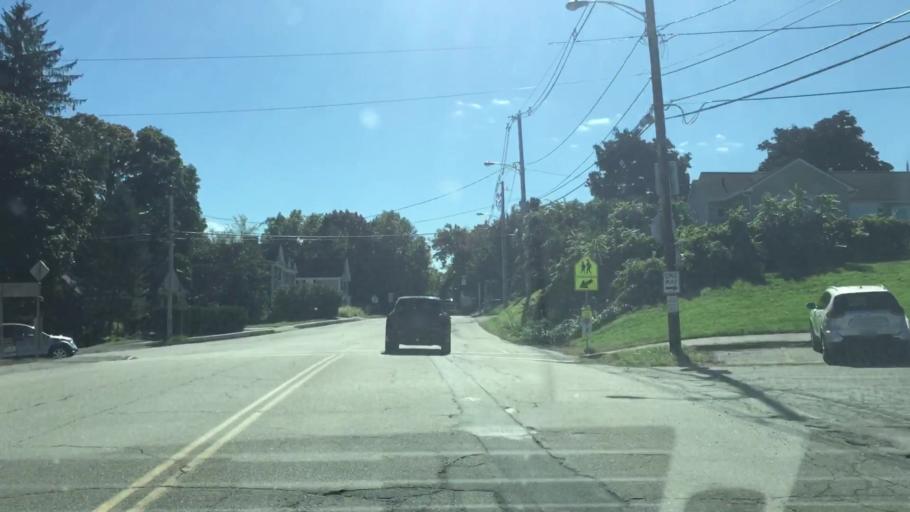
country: US
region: Massachusetts
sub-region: Essex County
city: North Andover
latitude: 42.6916
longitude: -71.1185
